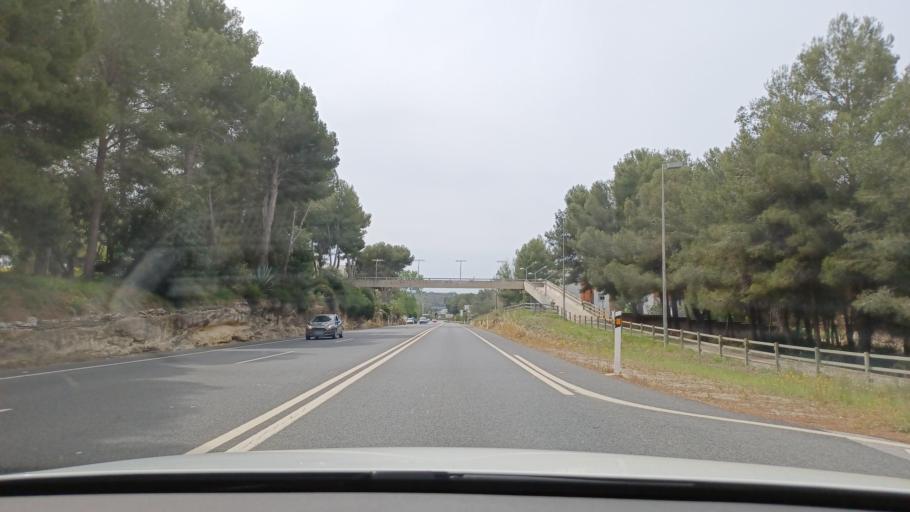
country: ES
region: Catalonia
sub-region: Provincia de Tarragona
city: Constanti
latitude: 41.1576
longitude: 1.2401
